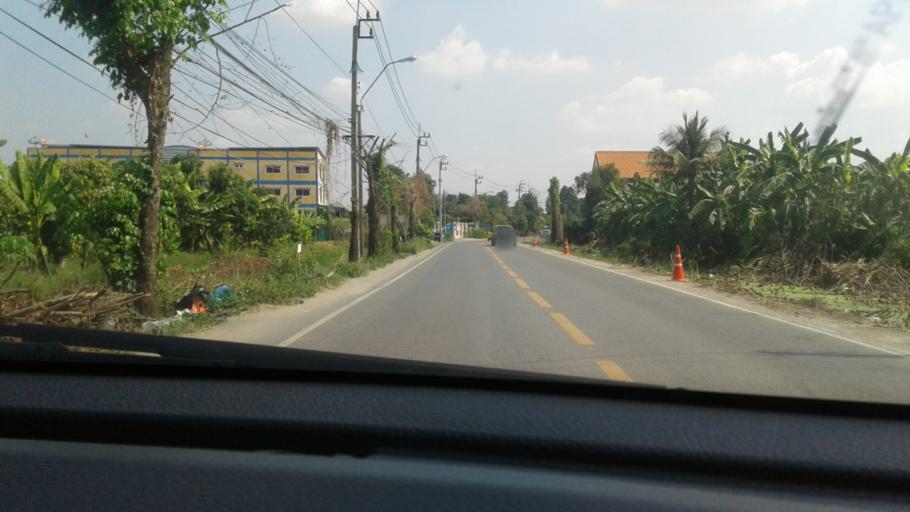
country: TH
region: Bangkok
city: Thawi Watthana
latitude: 13.7987
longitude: 100.3659
